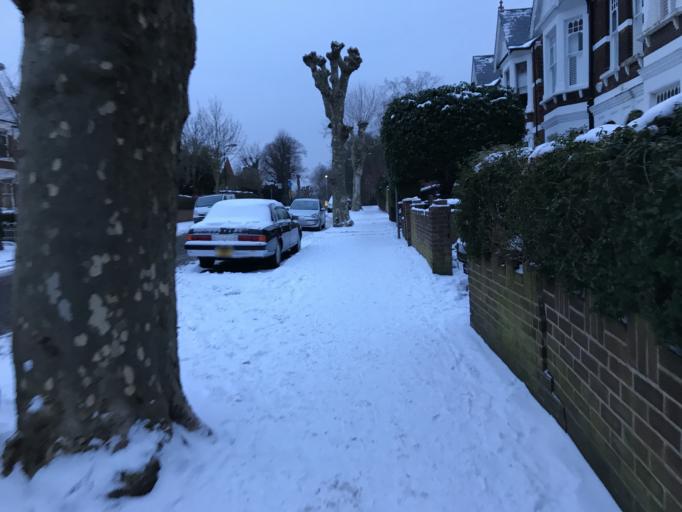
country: GB
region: England
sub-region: Greater London
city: Bayswater
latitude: 51.5358
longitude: -0.2151
